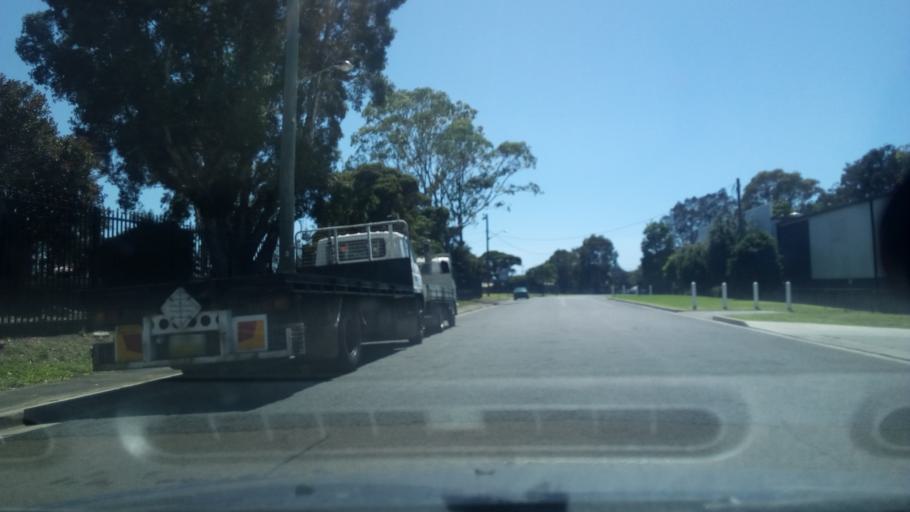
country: AU
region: New South Wales
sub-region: Wollongong
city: Coniston
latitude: -34.4382
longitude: 150.8885
